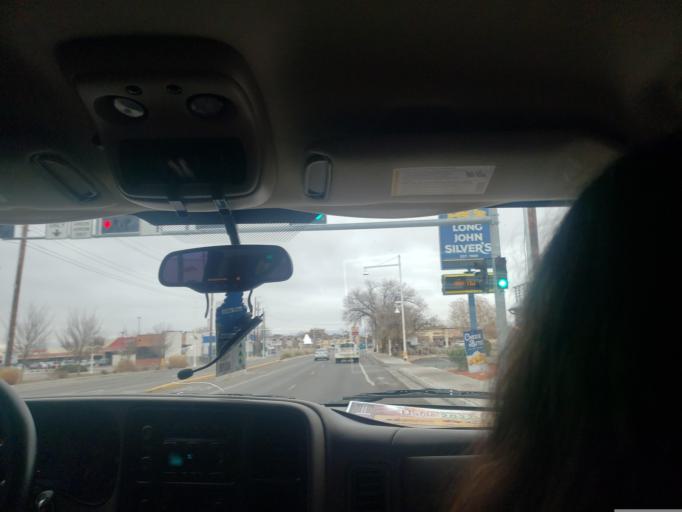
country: US
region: New Mexico
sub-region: Bernalillo County
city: Albuquerque
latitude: 35.0876
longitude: -106.6867
